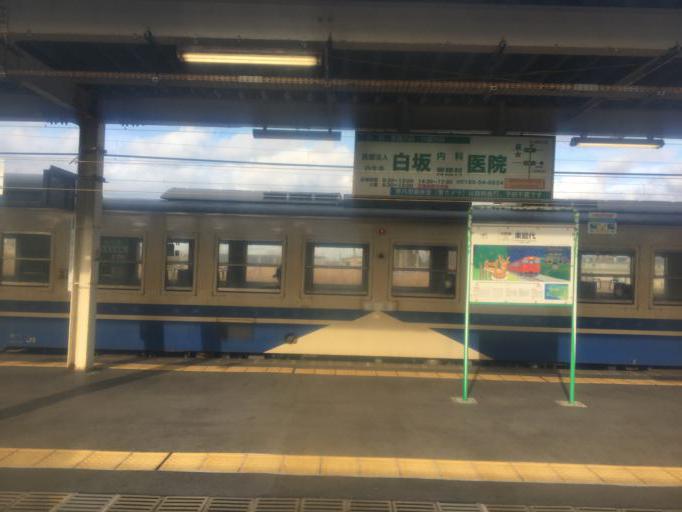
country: JP
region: Akita
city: Noshiromachi
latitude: 40.1916
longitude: 140.0658
